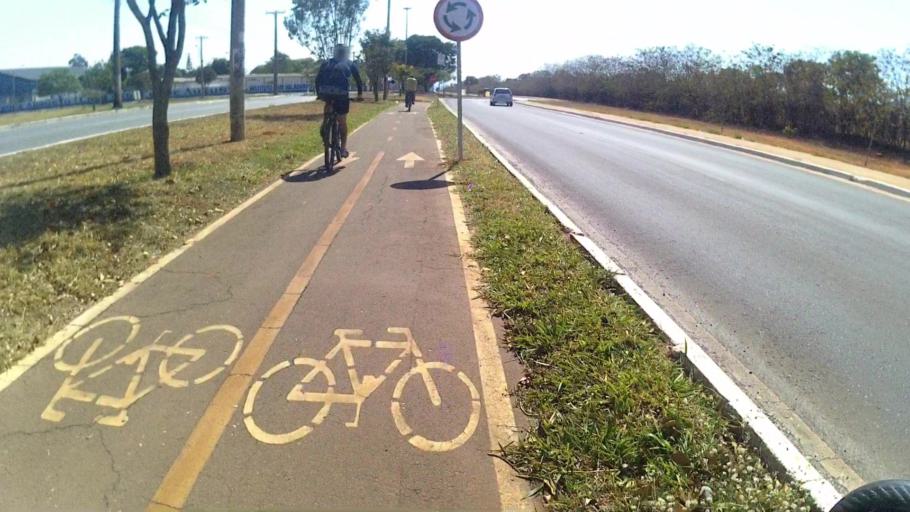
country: BR
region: Federal District
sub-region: Brasilia
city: Brasilia
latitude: -15.9067
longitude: -48.0472
